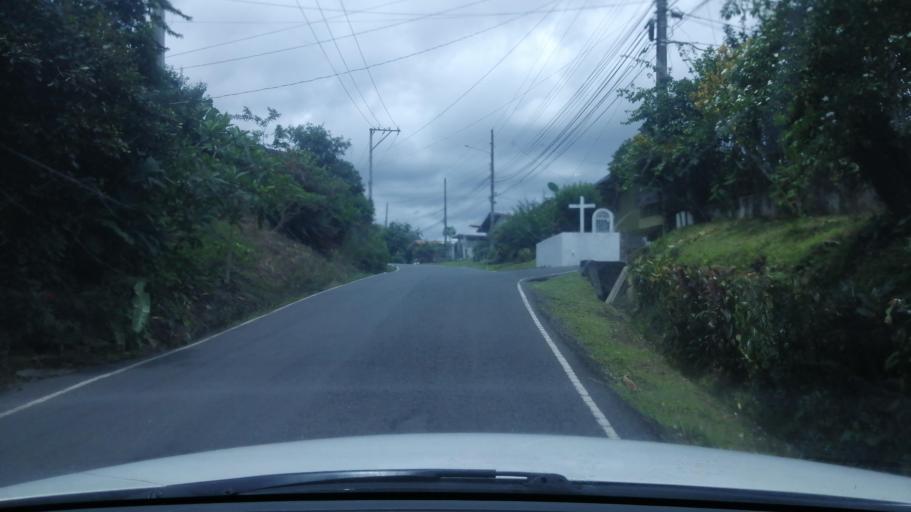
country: PA
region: Chiriqui
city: David
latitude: 8.4287
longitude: -82.4211
